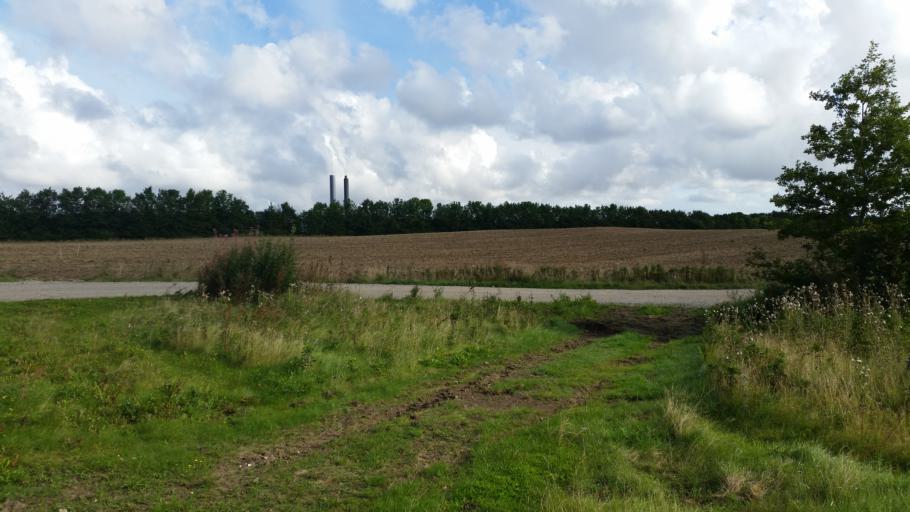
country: DK
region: Central Jutland
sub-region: Arhus Kommune
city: Trige
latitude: 56.2199
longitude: 10.1535
